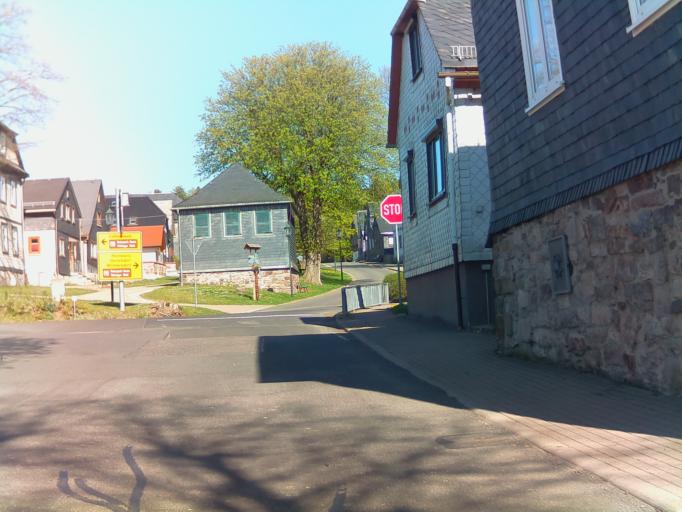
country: DE
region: Thuringia
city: Gillersdorf
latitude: 50.6062
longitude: 11.0174
